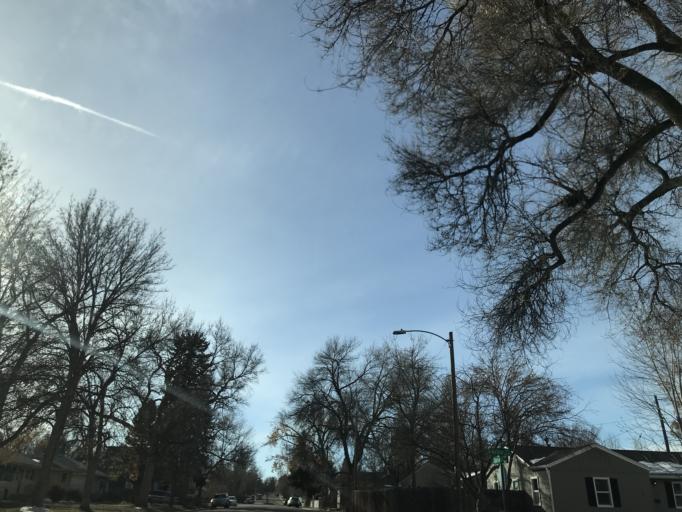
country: US
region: Colorado
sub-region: Arapahoe County
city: Littleton
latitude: 39.6037
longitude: -105.0116
